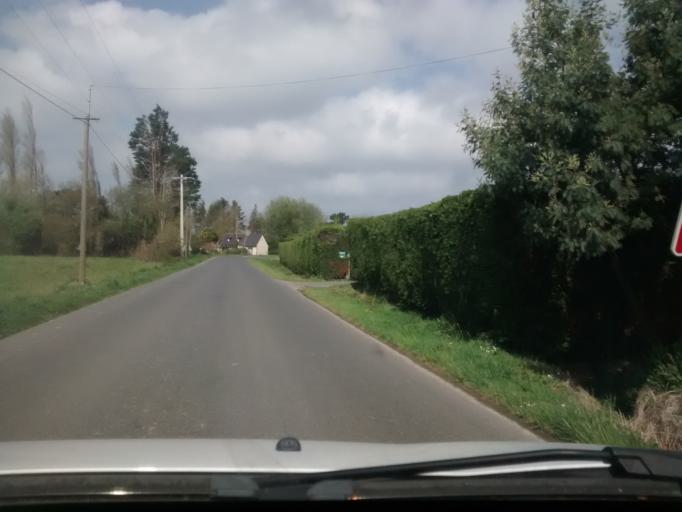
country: FR
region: Brittany
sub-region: Departement des Cotes-d'Armor
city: Trevou-Treguignec
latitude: 48.7907
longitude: -3.3430
